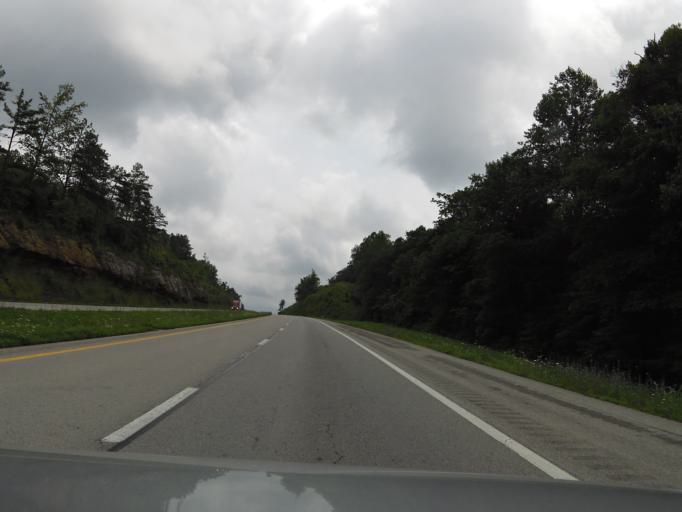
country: US
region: Kentucky
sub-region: Ohio County
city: Oak Grove
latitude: 37.3874
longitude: -86.6916
